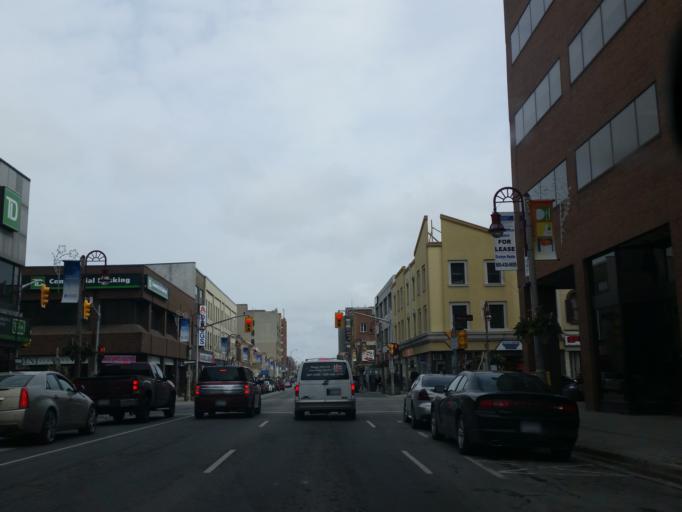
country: CA
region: Ontario
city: Oshawa
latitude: 43.8975
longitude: -78.8639
